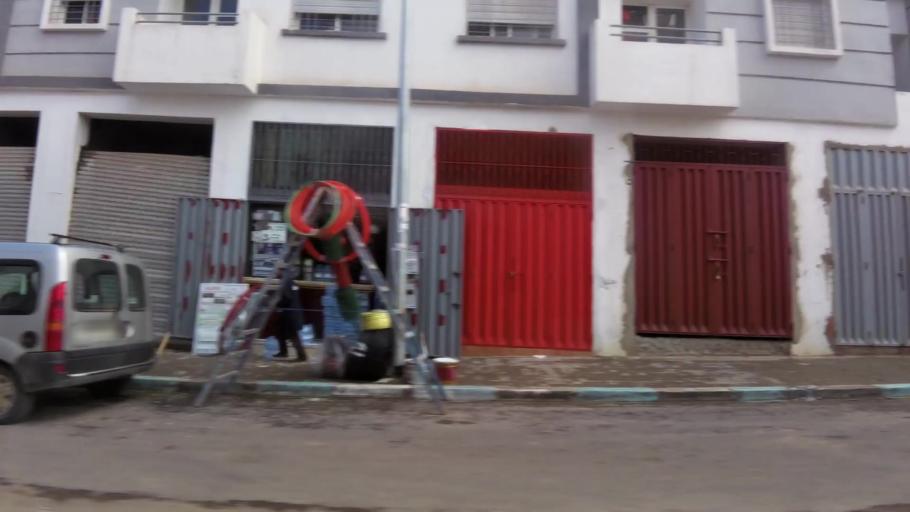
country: MA
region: Grand Casablanca
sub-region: Nouaceur
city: Dar Bouazza
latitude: 33.5334
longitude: -7.7196
